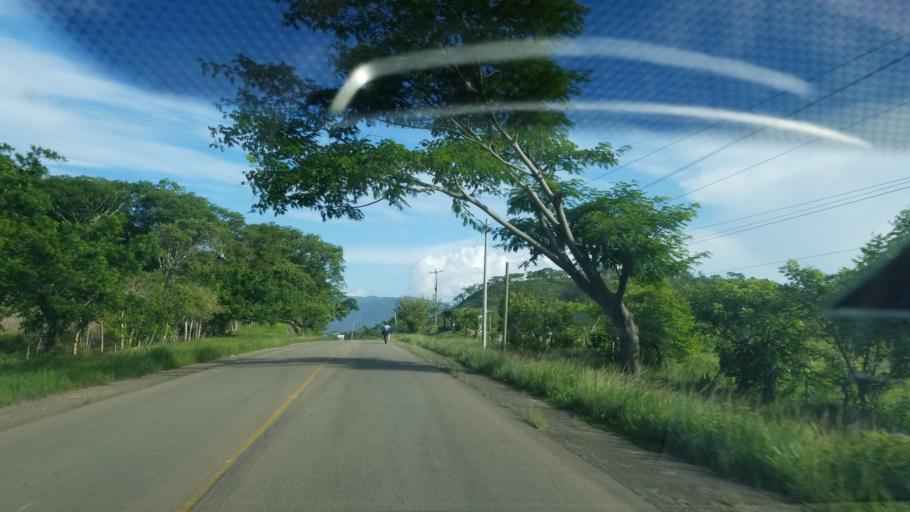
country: HN
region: El Paraiso
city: Arauli
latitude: 13.9180
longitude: -86.5576
